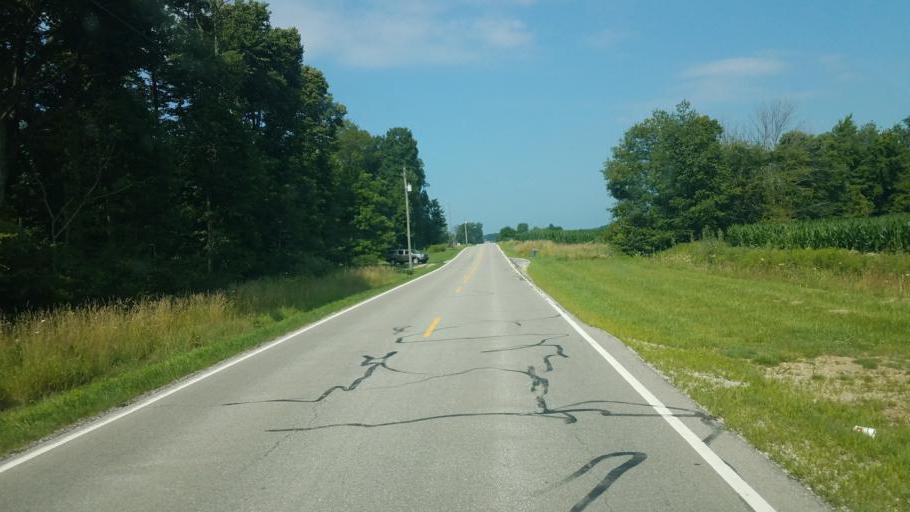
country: US
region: Ohio
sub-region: Crawford County
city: Galion
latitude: 40.7561
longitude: -82.8294
